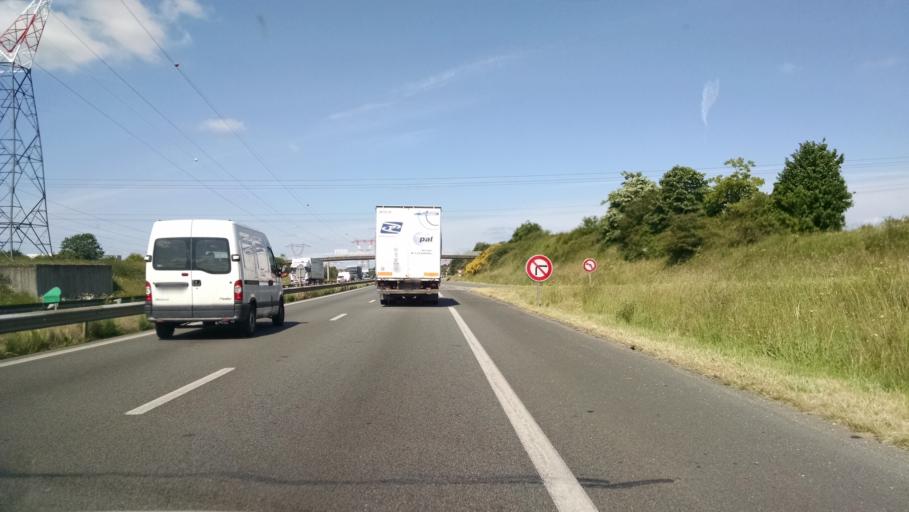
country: FR
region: Pays de la Loire
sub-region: Departement de la Loire-Atlantique
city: Reze
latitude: 47.1698
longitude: -1.5816
